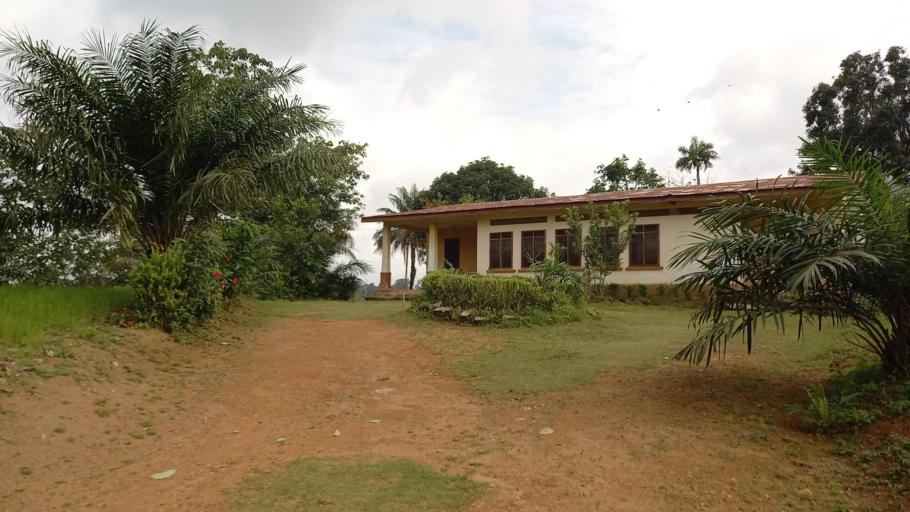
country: SL
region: Eastern Province
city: Kailahun
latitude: 8.2865
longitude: -10.5746
